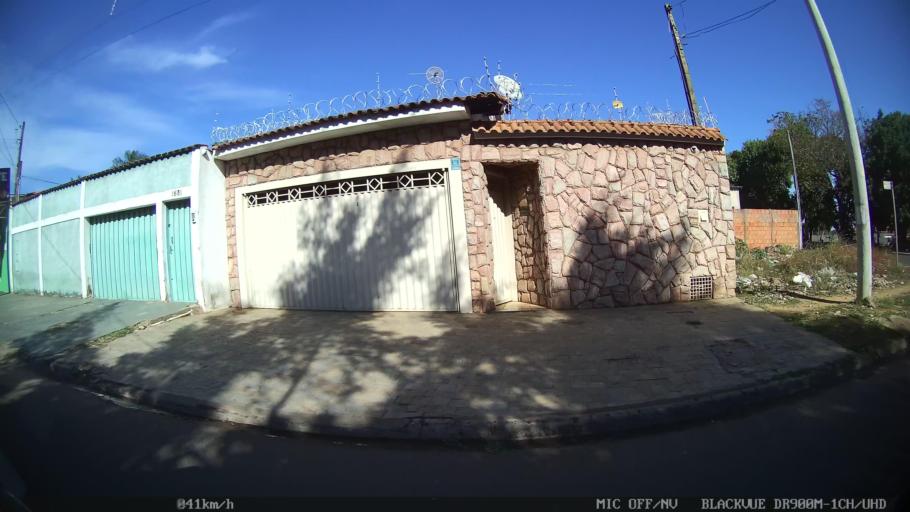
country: BR
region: Sao Paulo
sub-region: Franca
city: Franca
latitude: -20.4869
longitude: -47.4191
